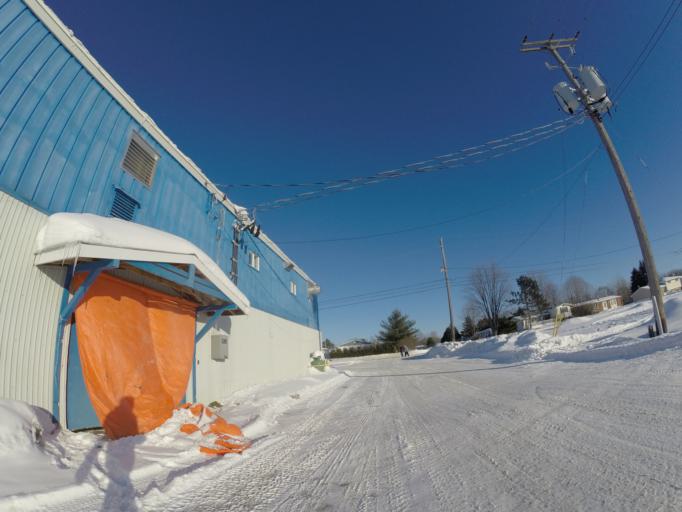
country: CA
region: Ontario
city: Rayside-Balfour
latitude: 46.5746
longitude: -81.1926
